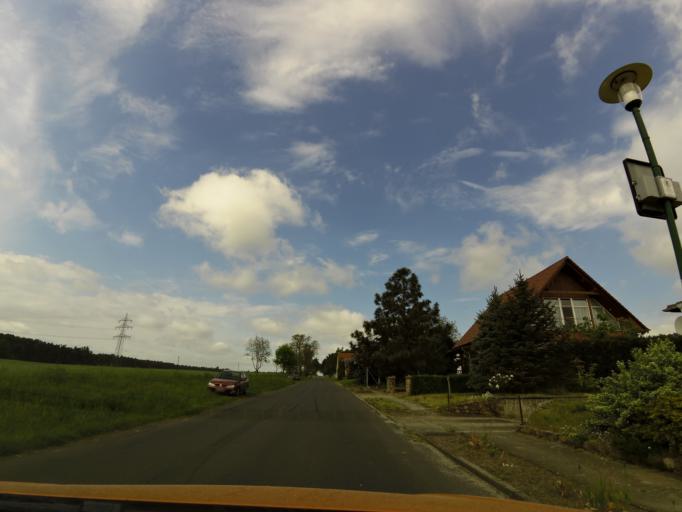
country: DE
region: Brandenburg
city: Belzig
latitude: 52.0969
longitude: 12.6171
